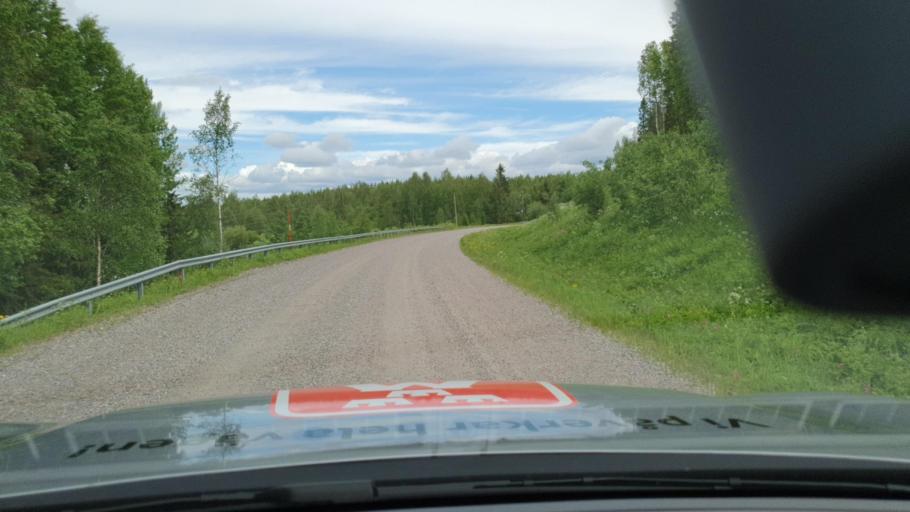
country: FI
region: Lapland
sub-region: Torniolaakso
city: Ylitornio
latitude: 65.9929
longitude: 23.7948
